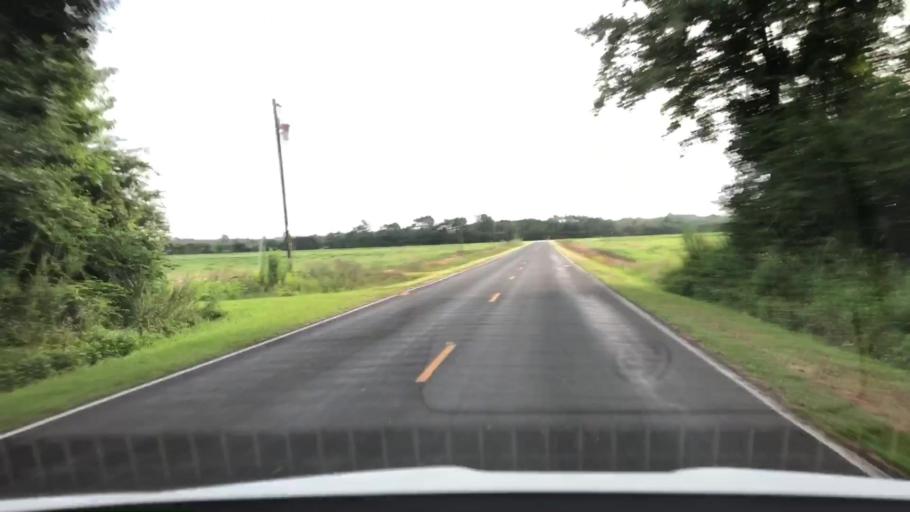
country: US
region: North Carolina
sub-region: Jones County
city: Trenton
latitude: 34.9985
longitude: -77.2770
